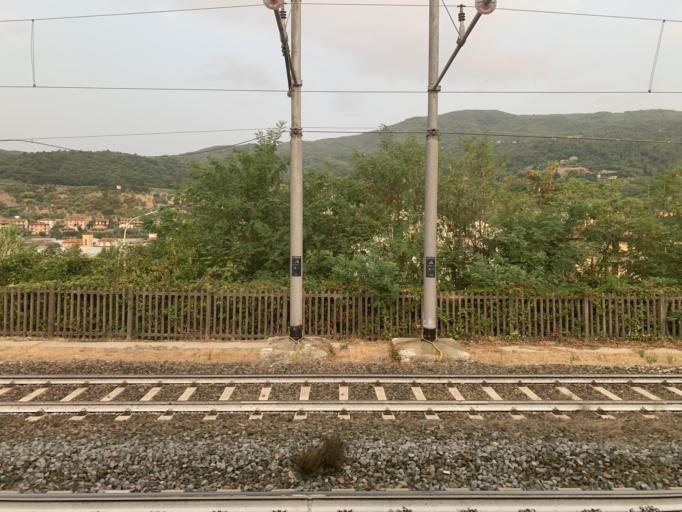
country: IT
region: Tuscany
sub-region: Provincia di Prato
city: Vaiano
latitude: 43.9602
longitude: 11.1309
